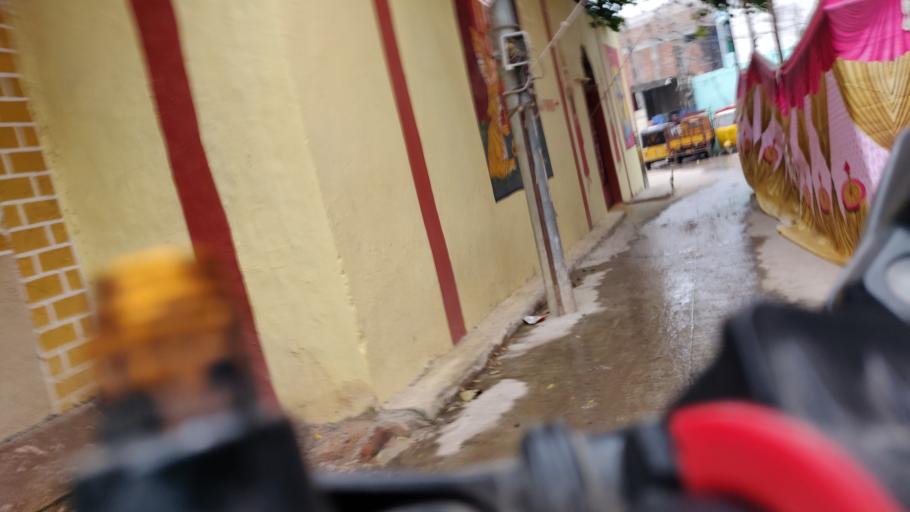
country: IN
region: Telangana
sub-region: Rangareddi
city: Kukatpalli
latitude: 17.4530
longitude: 78.4121
